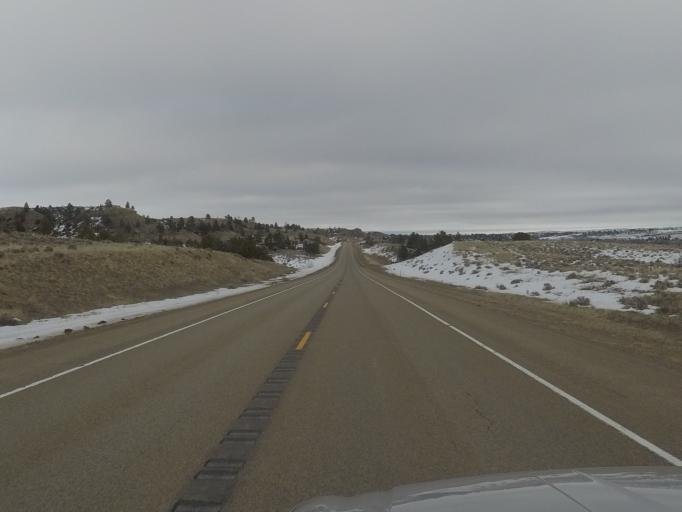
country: US
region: Montana
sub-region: Golden Valley County
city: Ryegate
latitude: 46.3170
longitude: -109.1471
